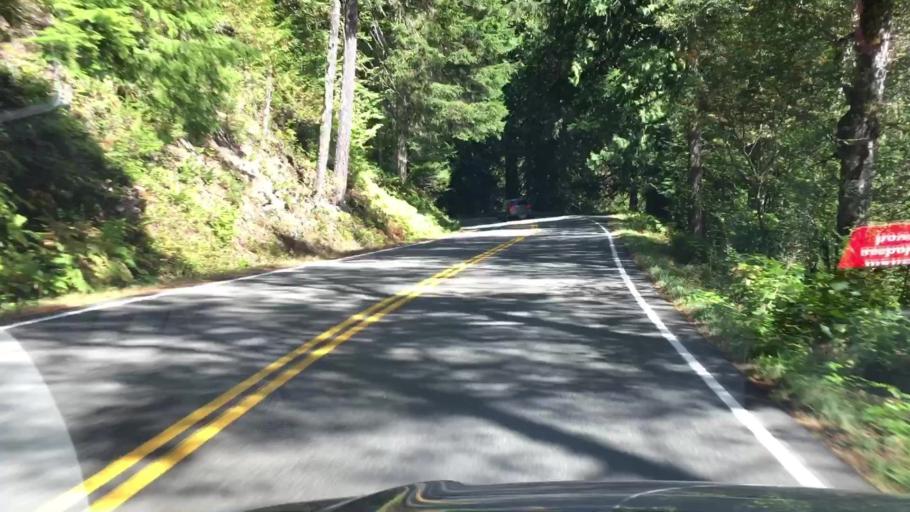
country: US
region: Washington
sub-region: Pierce County
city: Eatonville
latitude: 46.7397
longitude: -121.9074
